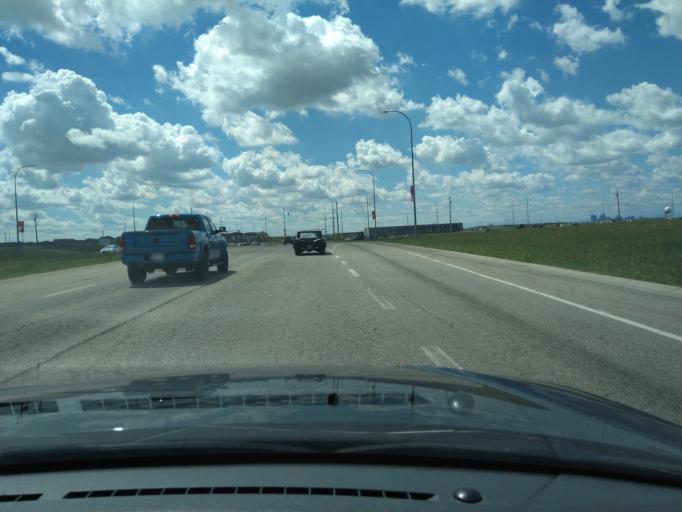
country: CA
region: Alberta
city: Calgary
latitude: 51.1562
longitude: -113.9702
